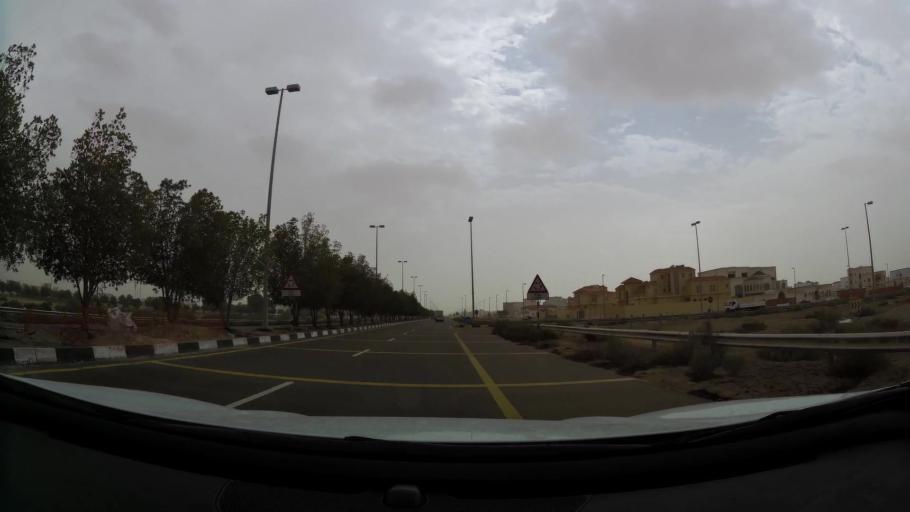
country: AE
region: Abu Dhabi
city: Abu Dhabi
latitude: 24.3760
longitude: 54.6948
